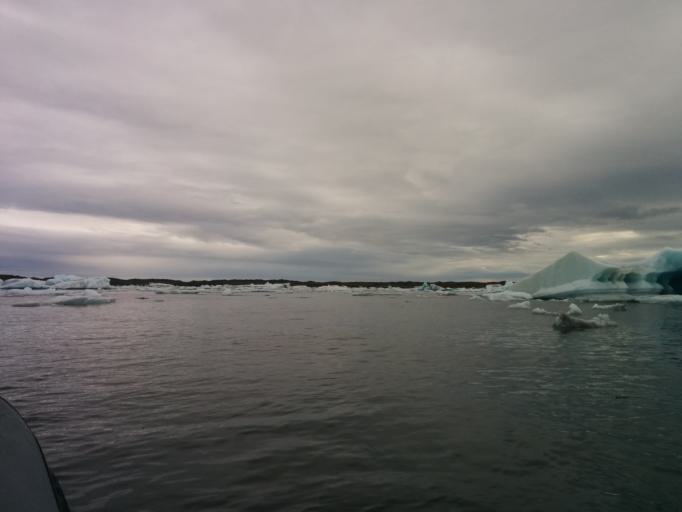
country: IS
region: East
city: Hoefn
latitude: 64.0589
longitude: -16.2066
